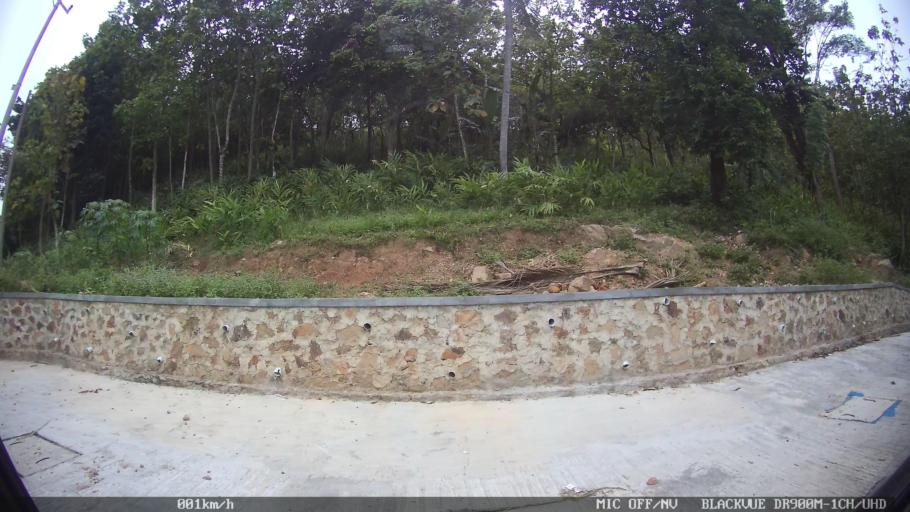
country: ID
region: Lampung
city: Bandarlampung
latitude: -5.4278
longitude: 105.3027
